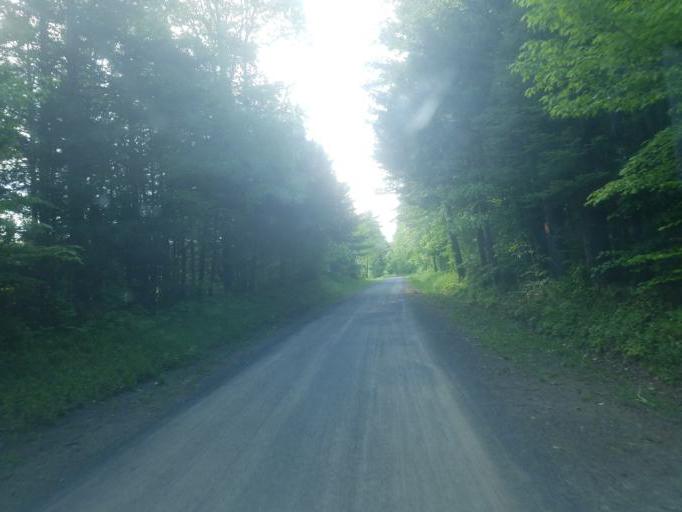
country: US
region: New York
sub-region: Herkimer County
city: Dolgeville
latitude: 43.3756
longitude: -74.9142
